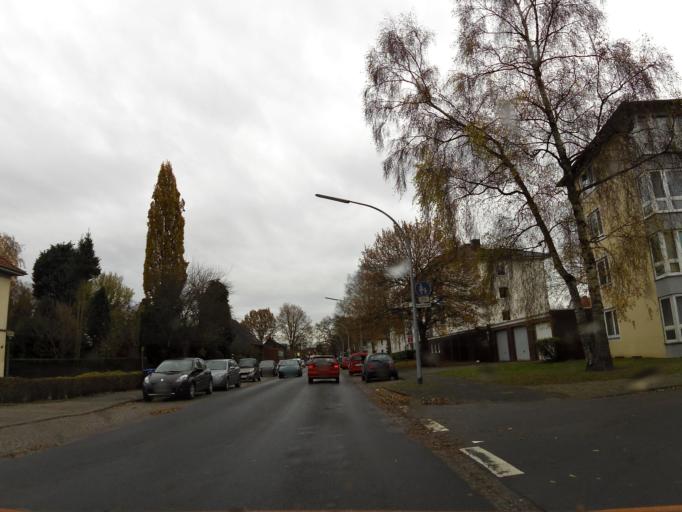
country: DE
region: Lower Saxony
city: Oldenburg
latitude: 53.1171
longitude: 8.2177
